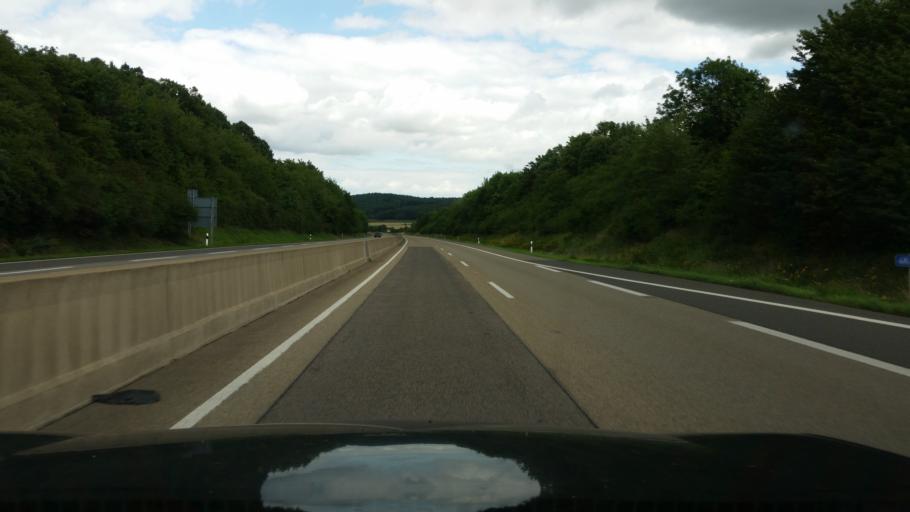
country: DE
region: North Rhine-Westphalia
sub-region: Regierungsbezirk Koln
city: Mechernich
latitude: 50.6112
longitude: 6.7126
